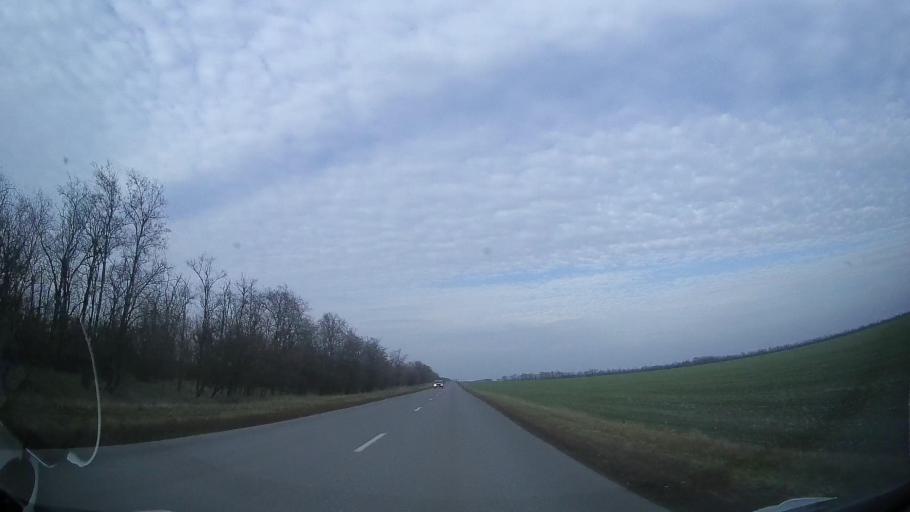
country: RU
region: Rostov
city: Zernograd
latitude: 46.9185
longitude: 40.3389
